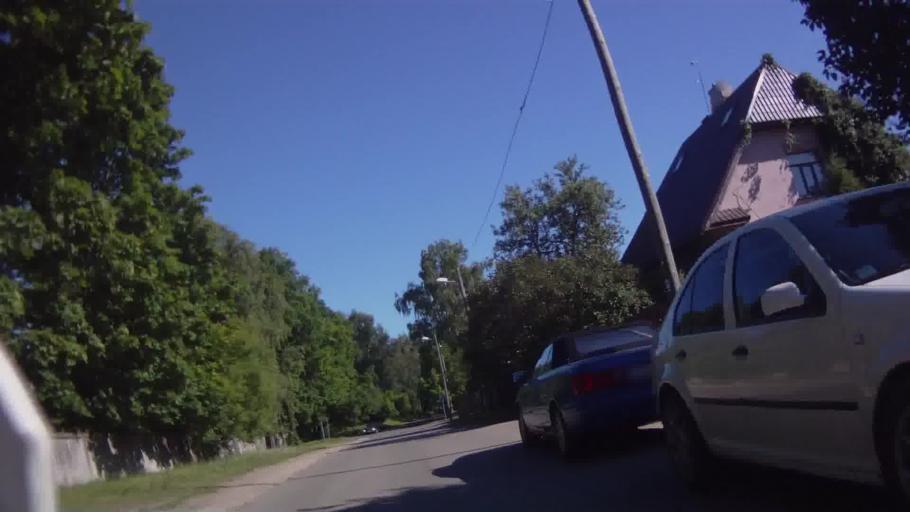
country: LV
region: Riga
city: Riga
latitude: 56.9132
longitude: 24.1061
